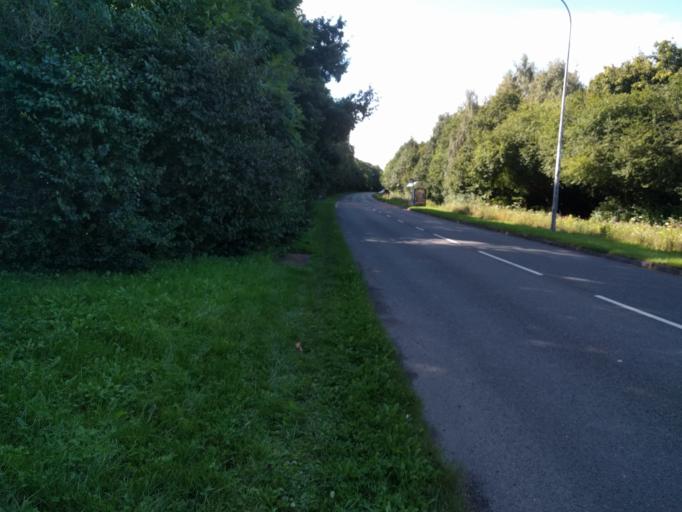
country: GB
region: England
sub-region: Warrington
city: Culcheth
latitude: 53.4250
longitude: -2.5075
